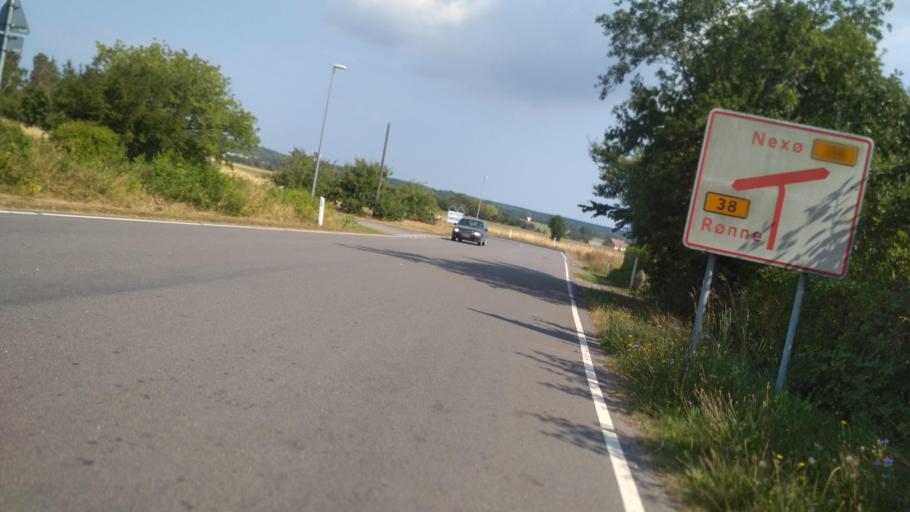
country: DK
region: Capital Region
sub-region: Bornholm Kommune
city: Akirkeby
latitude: 55.0710
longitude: 14.9278
